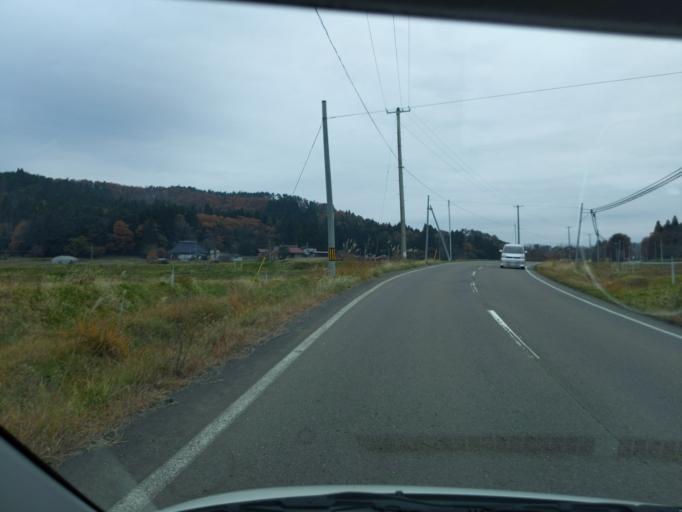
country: JP
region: Iwate
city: Kitakami
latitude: 39.2221
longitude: 141.2222
